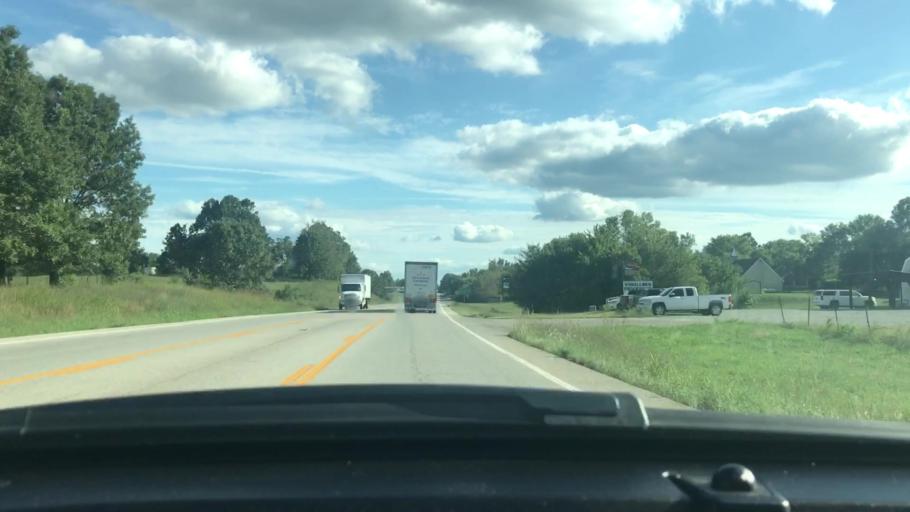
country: US
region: Missouri
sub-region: Oregon County
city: Thayer
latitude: 36.6022
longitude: -91.6440
